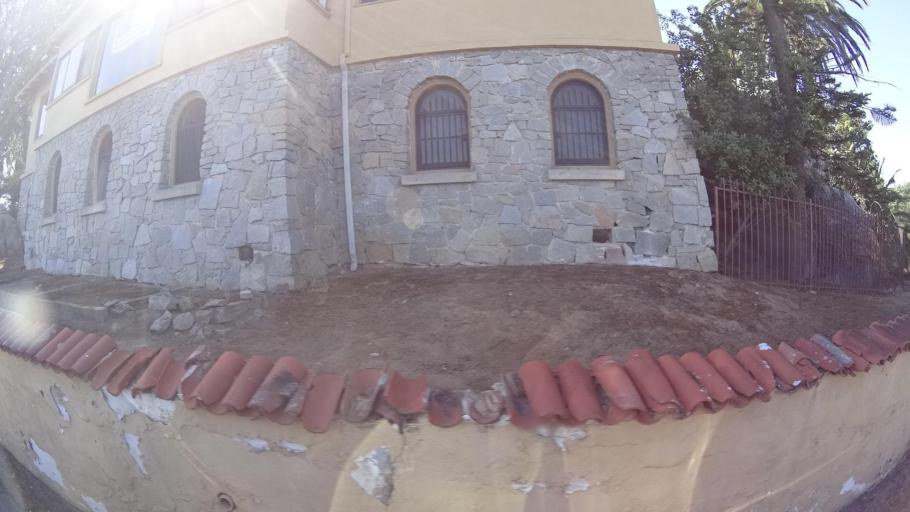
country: US
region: California
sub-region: San Diego County
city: Casa de Oro-Mount Helix
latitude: 32.7764
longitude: -116.9842
